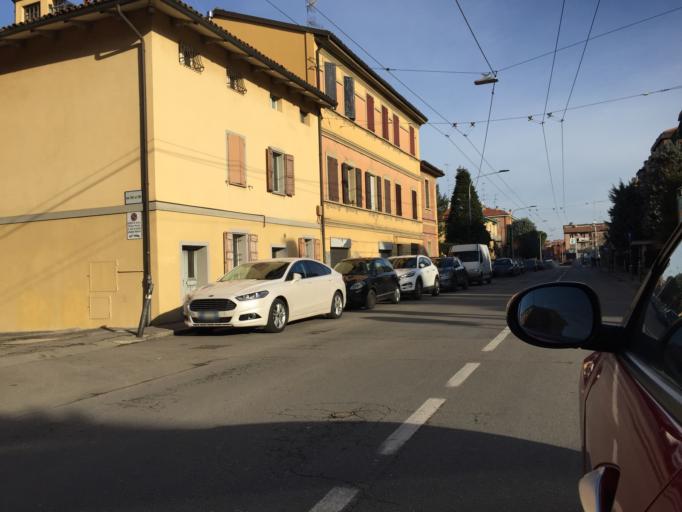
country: IT
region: Emilia-Romagna
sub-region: Provincia di Bologna
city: Casalecchio di Reno
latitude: 44.4957
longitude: 11.2945
